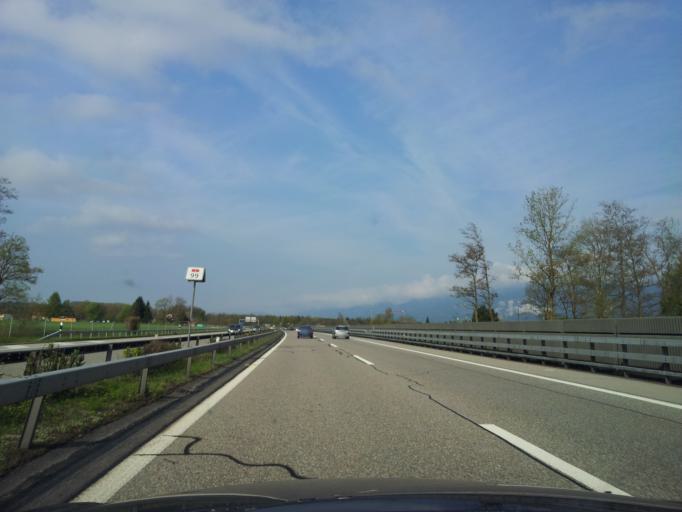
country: CH
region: Solothurn
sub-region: Bezirk Wasseramt
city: Luterbach
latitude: 47.2101
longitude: 7.5915
